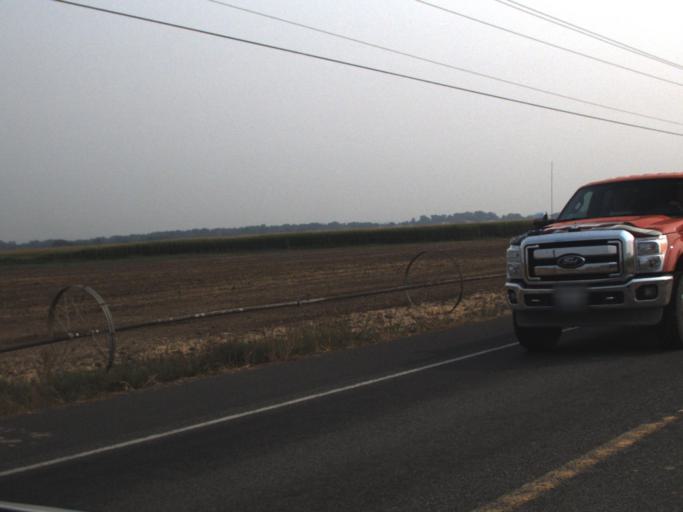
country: US
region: Washington
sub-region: Yakima County
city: Granger
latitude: 46.3284
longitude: -120.2260
